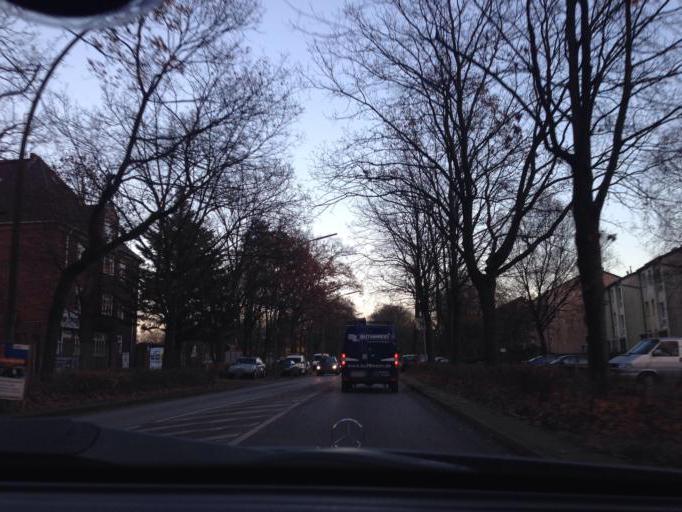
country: DE
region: Schleswig-Holstein
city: Barsbuettel
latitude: 53.6069
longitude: 10.1759
